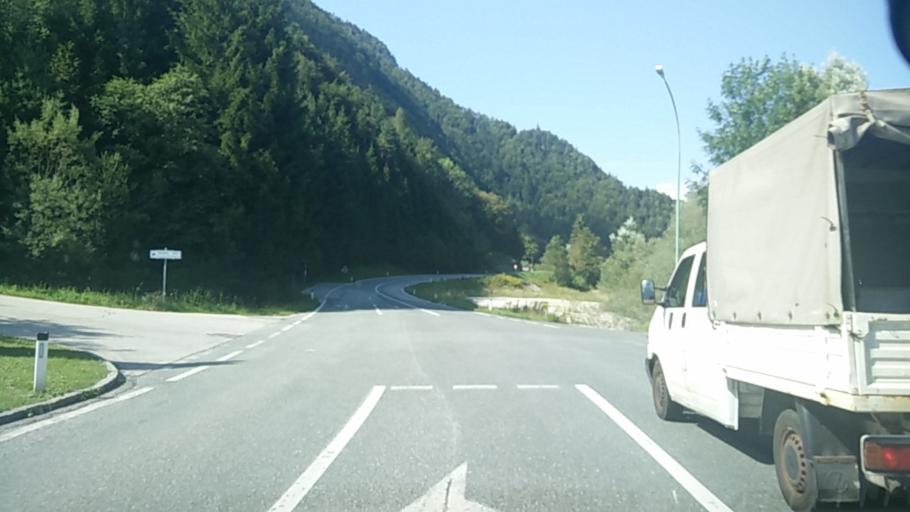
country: AT
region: Carinthia
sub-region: Politischer Bezirk Volkermarkt
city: Bad Eisenkappel
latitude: 46.5179
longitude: 14.5771
